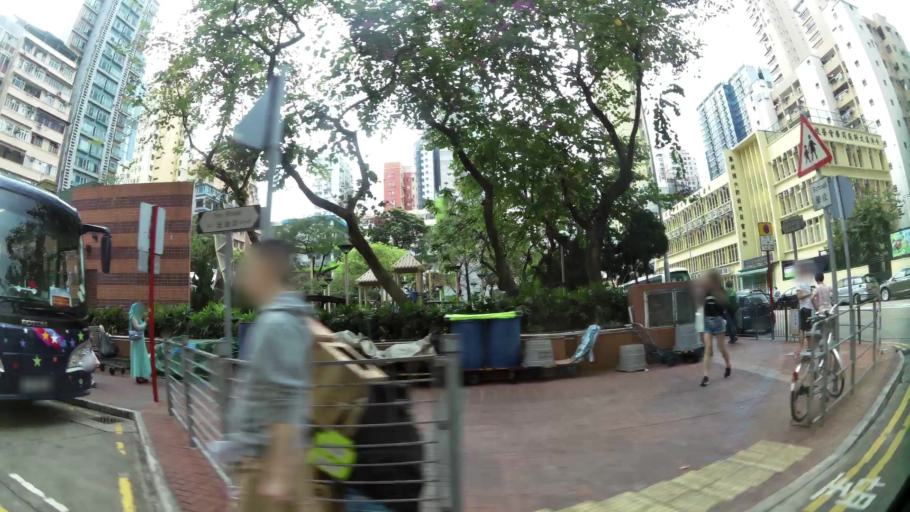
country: HK
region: Kowloon City
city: Kowloon
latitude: 22.3170
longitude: 114.1720
